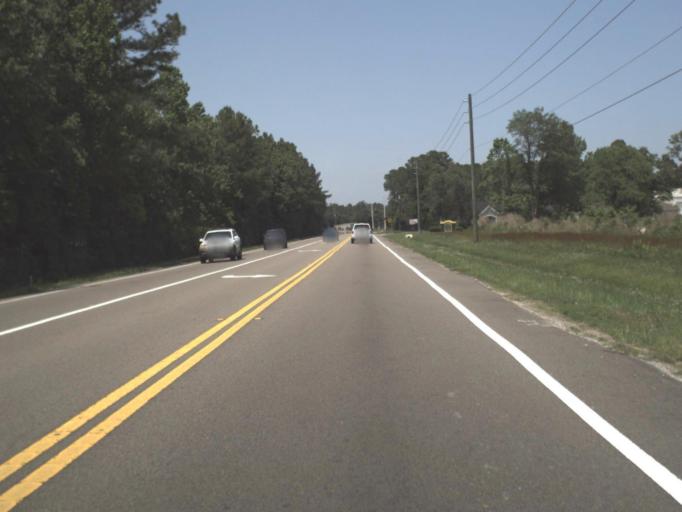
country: US
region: Florida
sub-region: Nassau County
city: Yulee
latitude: 30.4919
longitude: -81.6244
